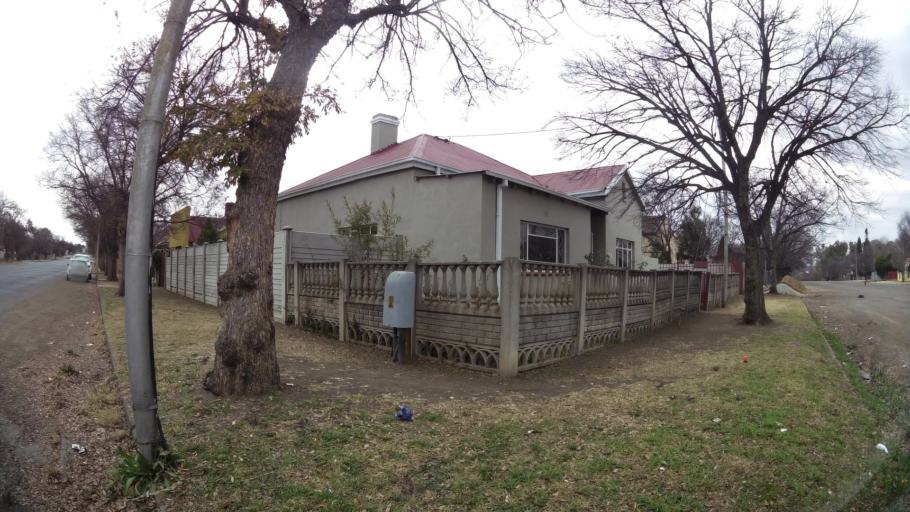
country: ZA
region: Orange Free State
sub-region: Fezile Dabi District Municipality
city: Kroonstad
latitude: -27.6578
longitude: 27.2433
